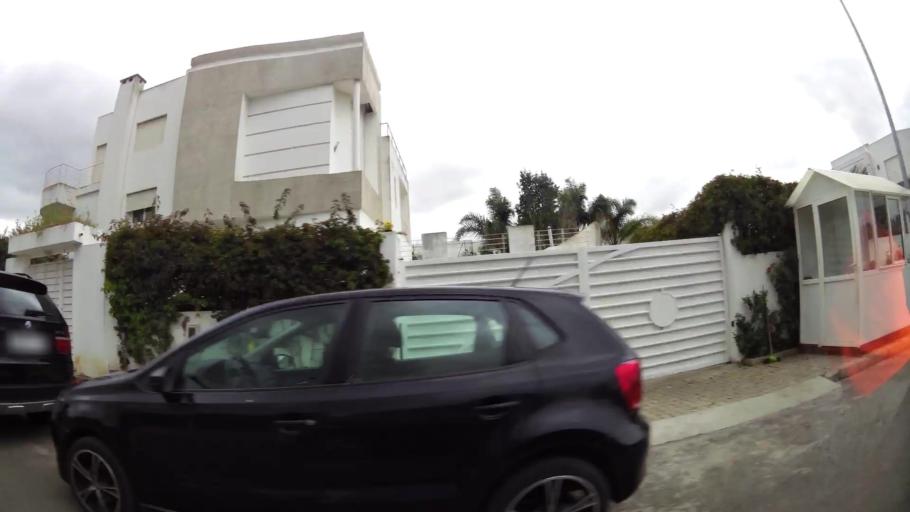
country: MA
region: Grand Casablanca
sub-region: Casablanca
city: Casablanca
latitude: 33.5346
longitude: -7.6336
